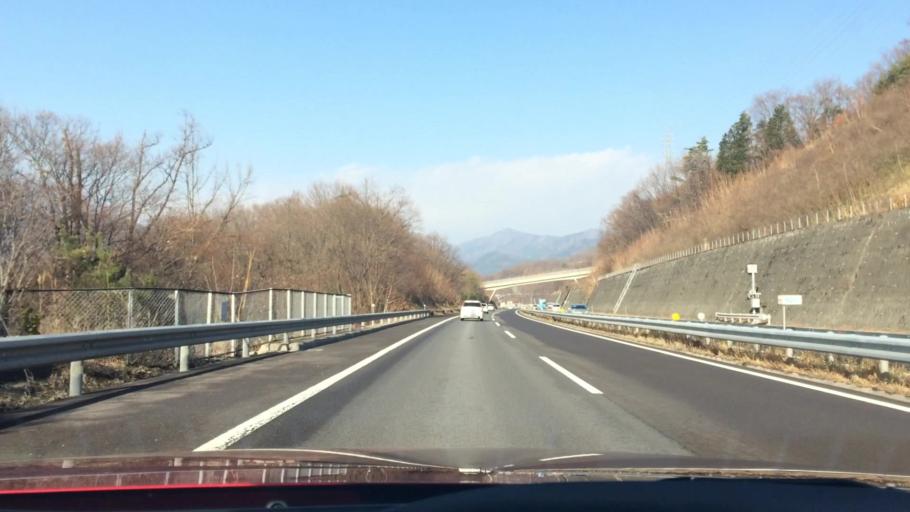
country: JP
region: Nagano
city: Ueda
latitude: 36.3923
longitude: 138.3130
